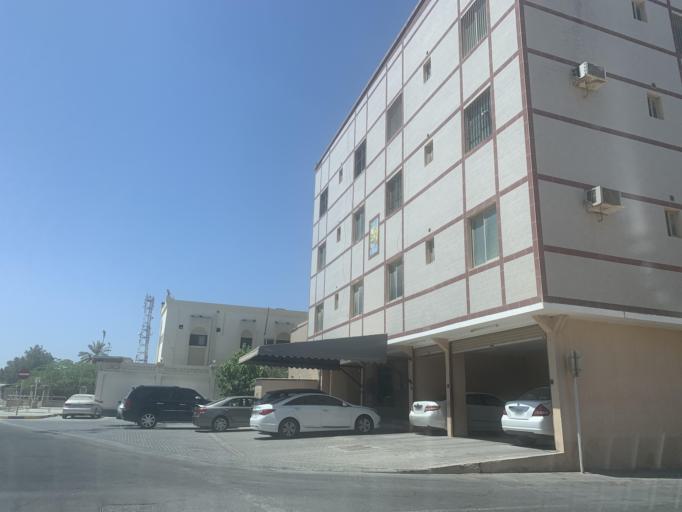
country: BH
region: Manama
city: Jidd Hafs
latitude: 26.2143
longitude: 50.4517
